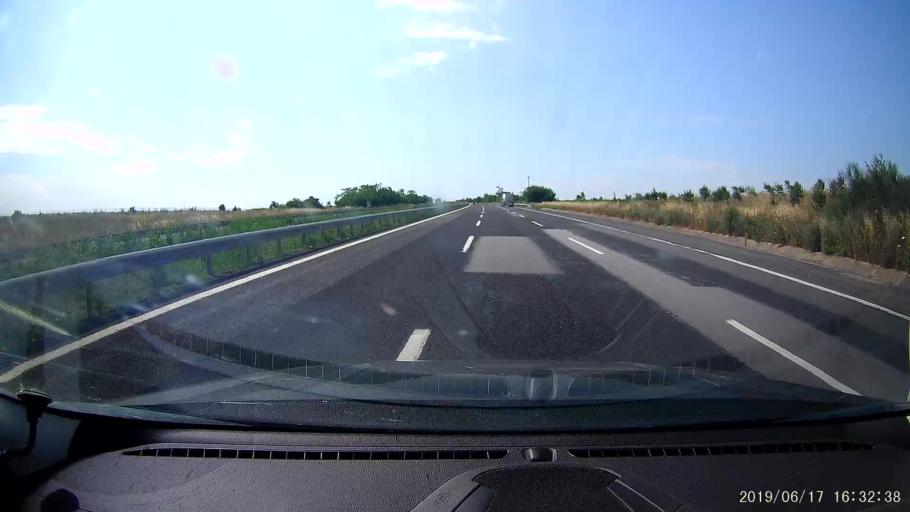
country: TR
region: Kirklareli
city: Buyukkaristiran
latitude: 41.3717
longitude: 27.5950
